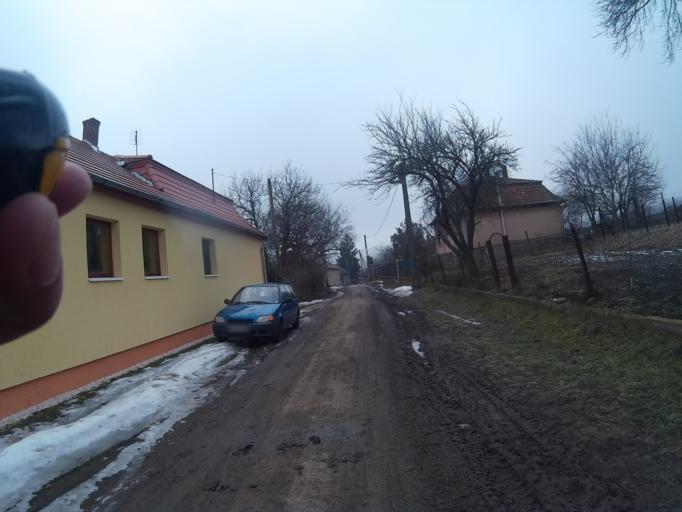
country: HU
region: Nograd
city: Tar
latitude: 47.9882
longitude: 19.7267
